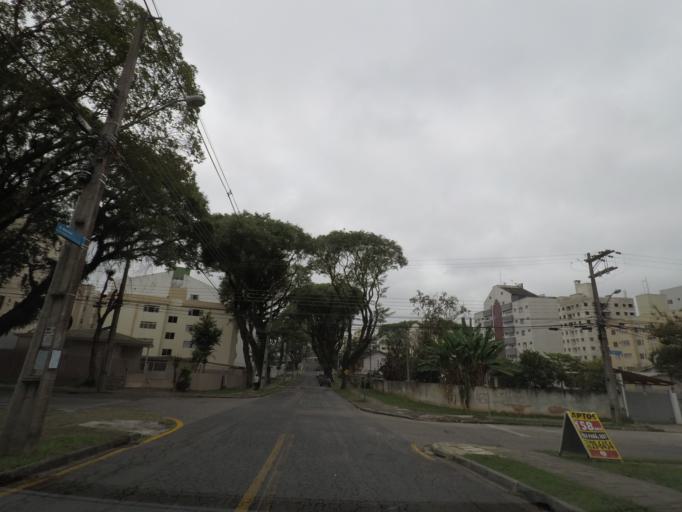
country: BR
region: Parana
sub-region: Curitiba
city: Curitiba
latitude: -25.4711
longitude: -49.2883
